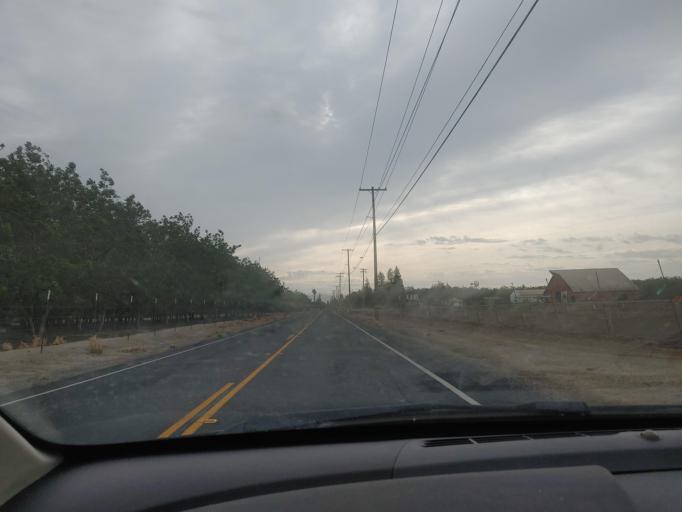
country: US
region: California
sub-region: Stanislaus County
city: Salida
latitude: 37.6817
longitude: -121.0773
